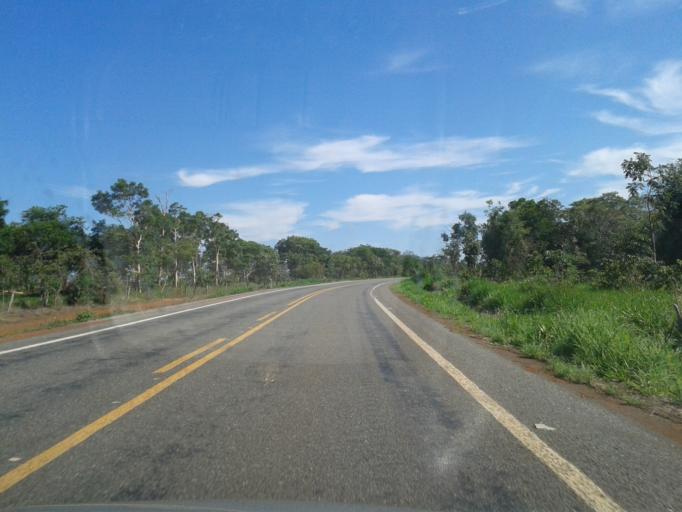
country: BR
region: Goias
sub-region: Piracanjuba
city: Piracanjuba
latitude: -17.2956
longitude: -48.7911
